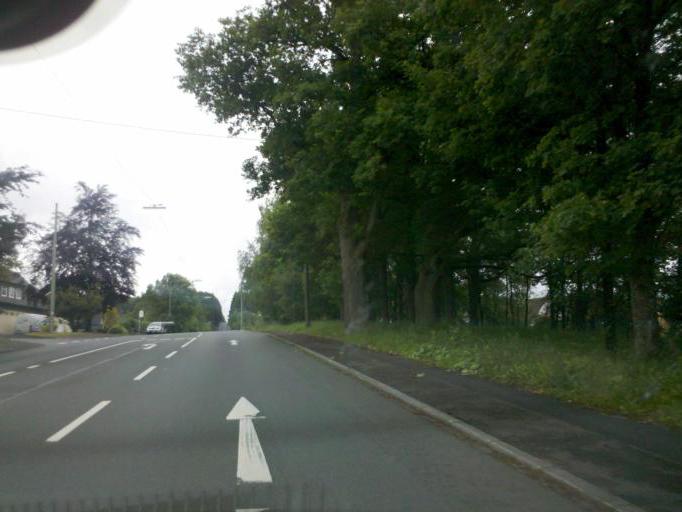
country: DE
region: North Rhine-Westphalia
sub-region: Regierungsbezirk Arnsberg
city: Wilnsdorf
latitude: 50.8100
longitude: 8.1080
